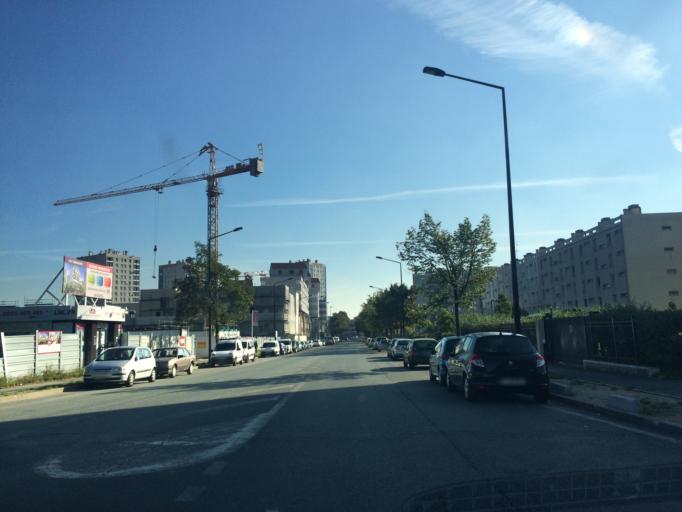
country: FR
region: Ile-de-France
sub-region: Departement du Val-de-Marne
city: Chennevieres-sur-Marne
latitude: 48.8068
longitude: 2.5359
